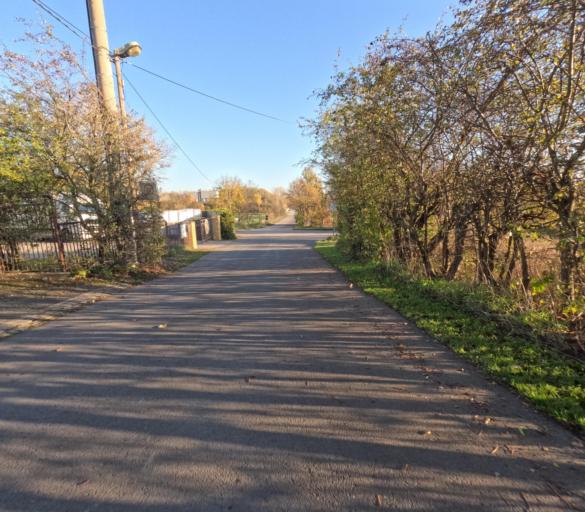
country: DE
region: Saxony
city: Otterwisch
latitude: 51.2517
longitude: 12.6459
